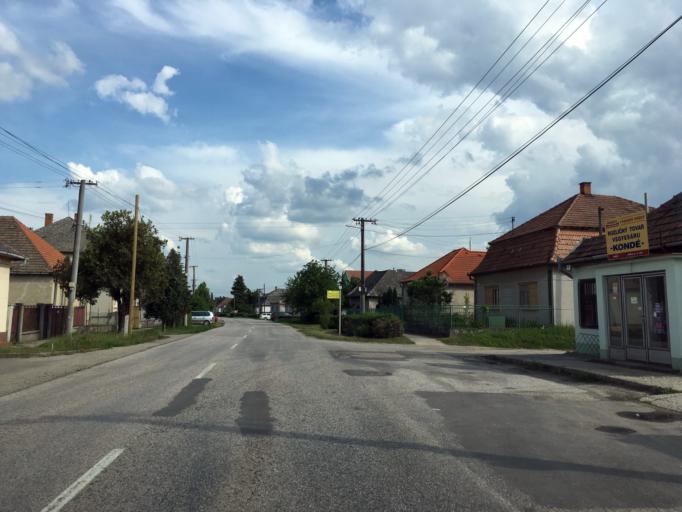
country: SK
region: Nitriansky
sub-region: Okres Komarno
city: Hurbanovo
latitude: 47.8034
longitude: 18.2339
